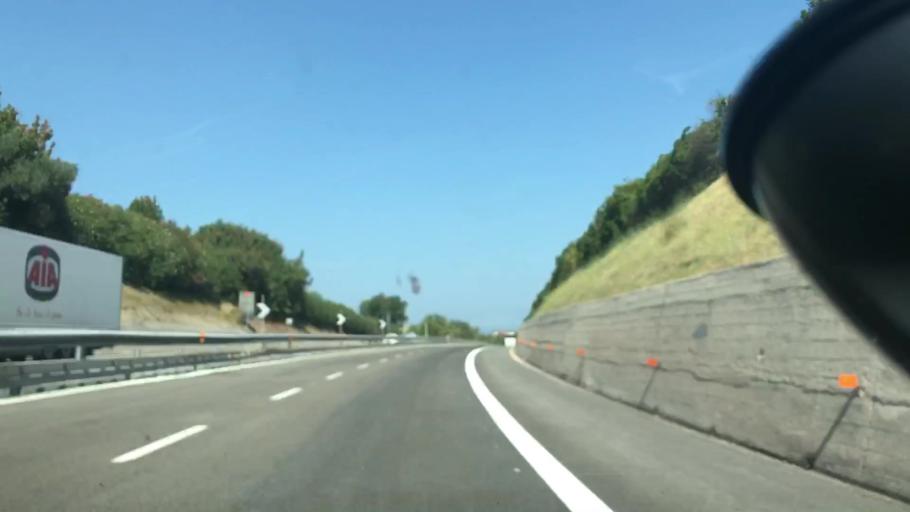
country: IT
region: Abruzzo
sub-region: Provincia di Chieti
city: San Vito Chietino
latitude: 42.3038
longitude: 14.4223
